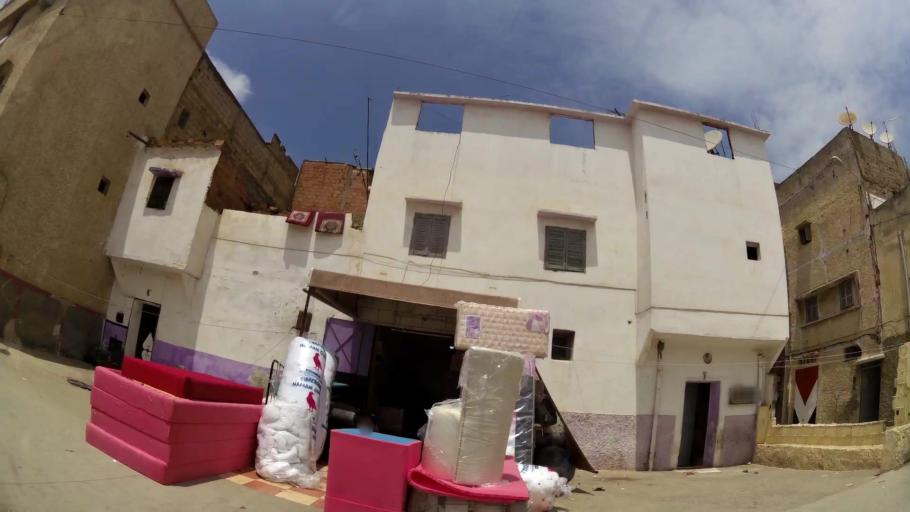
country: MA
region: Rabat-Sale-Zemmour-Zaer
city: Sale
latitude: 34.0510
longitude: -6.7897
